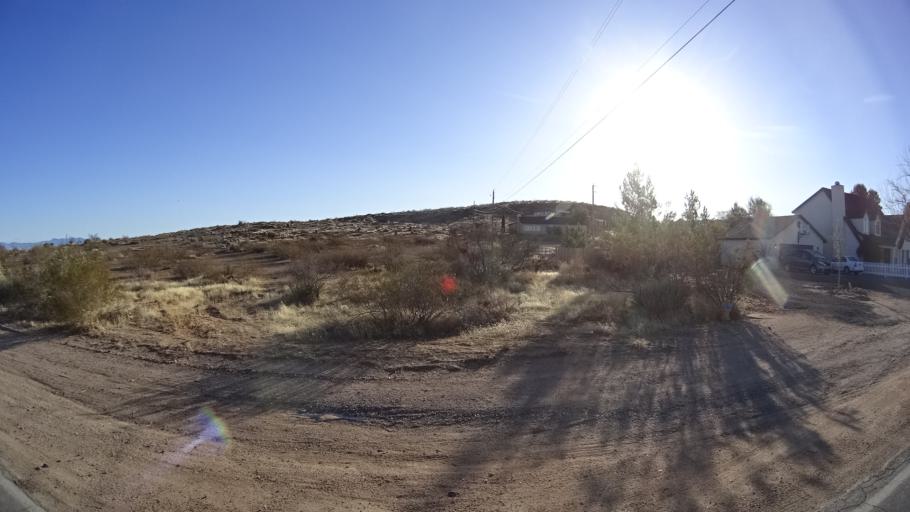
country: US
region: Arizona
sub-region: Mohave County
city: Kingman
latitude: 35.2089
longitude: -114.0114
